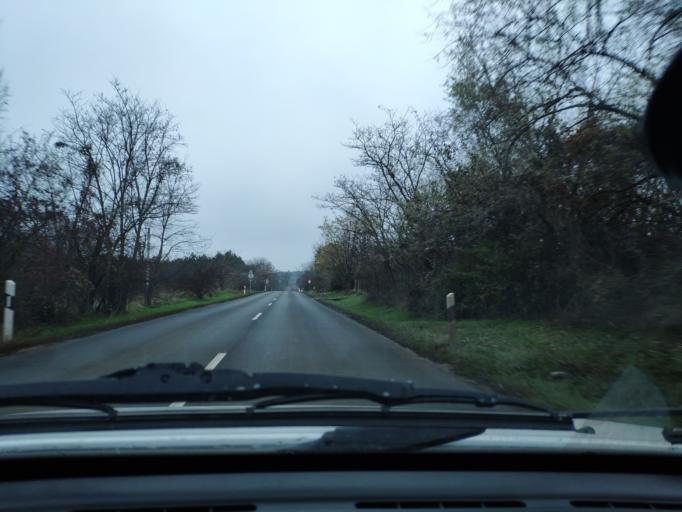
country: HU
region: Pest
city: Soskut
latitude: 47.4304
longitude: 18.8240
